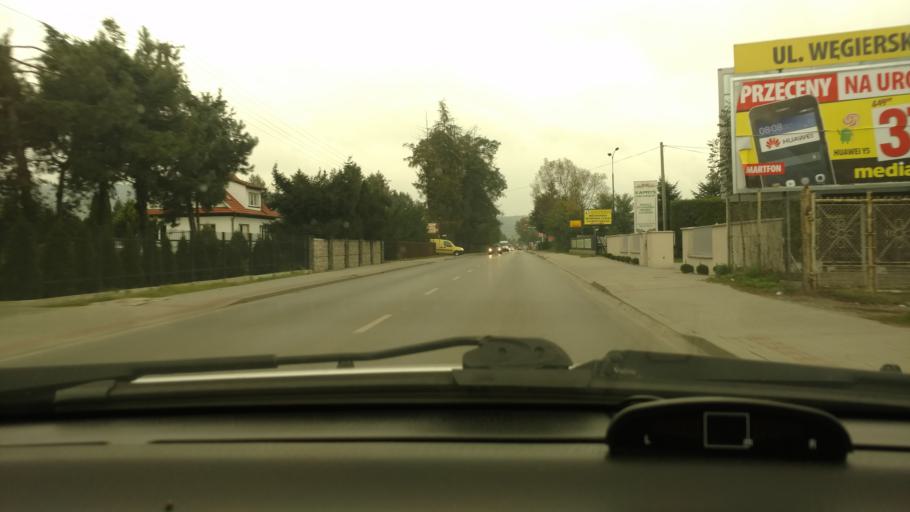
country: PL
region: Lesser Poland Voivodeship
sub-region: Powiat nowosadecki
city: Chelmiec
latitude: 49.6262
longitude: 20.6679
